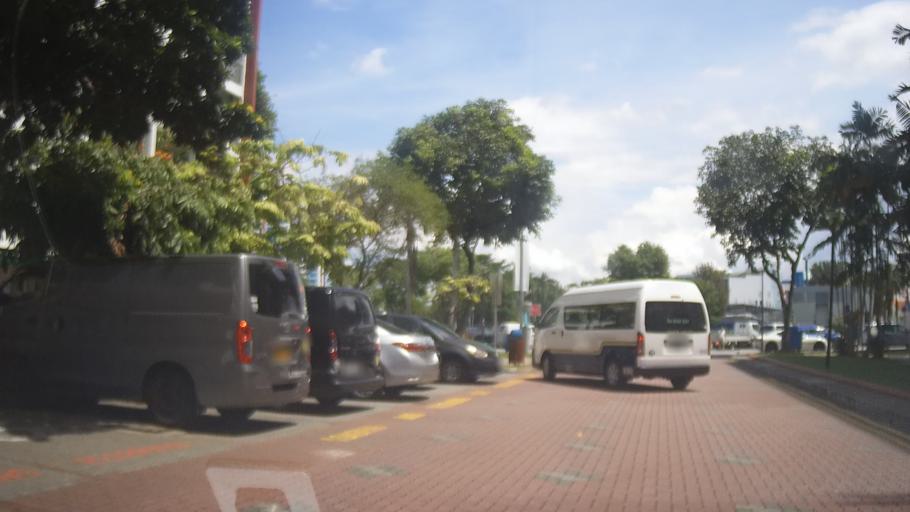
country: SG
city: Singapore
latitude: 1.3246
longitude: 103.8855
